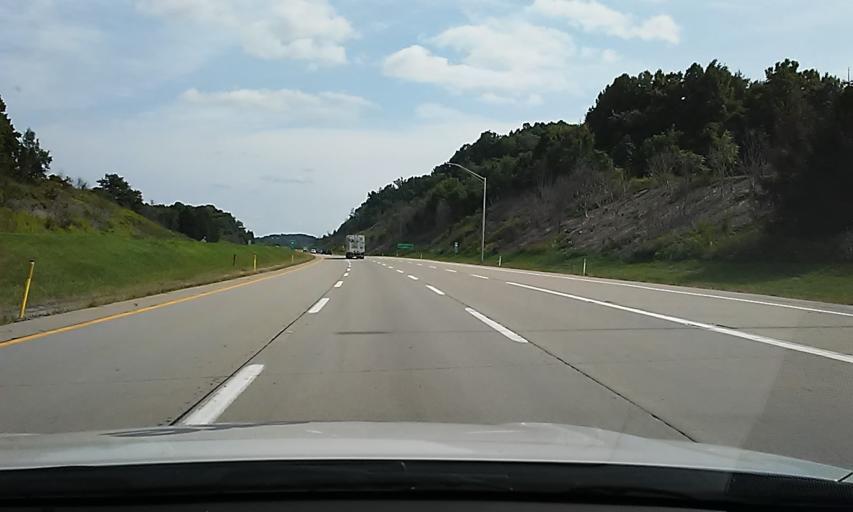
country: US
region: Pennsylvania
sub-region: Westmoreland County
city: Delmont
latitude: 40.3798
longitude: -79.5656
